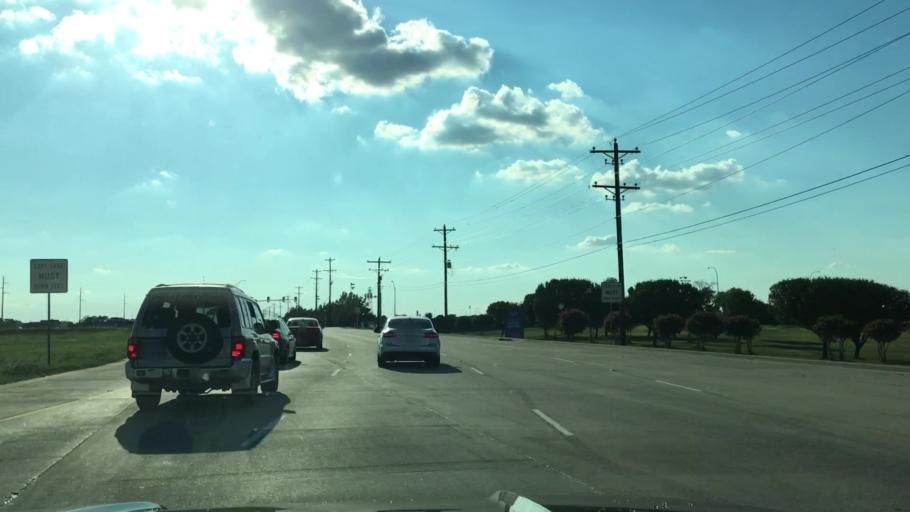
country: US
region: Texas
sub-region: Denton County
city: Roanoke
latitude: 33.0271
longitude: -97.2764
